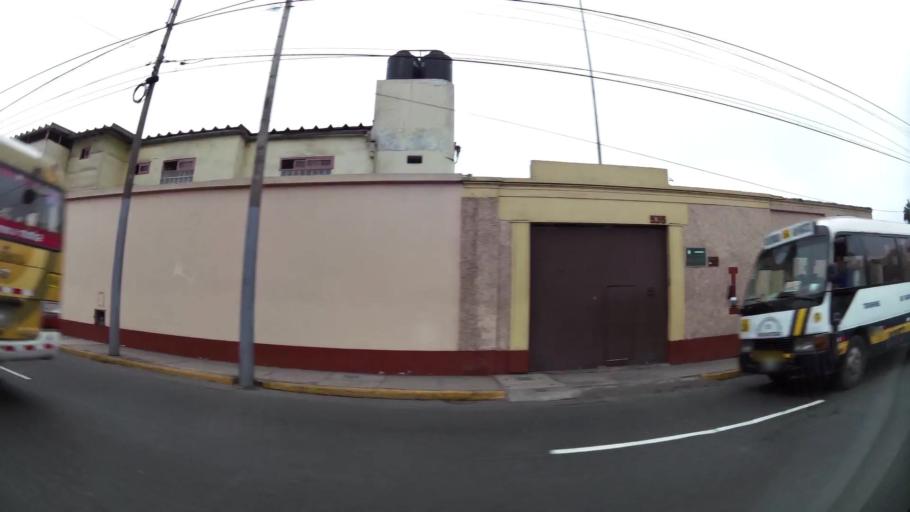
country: PE
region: Callao
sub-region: Callao
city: Callao
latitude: -12.0880
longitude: -77.0879
